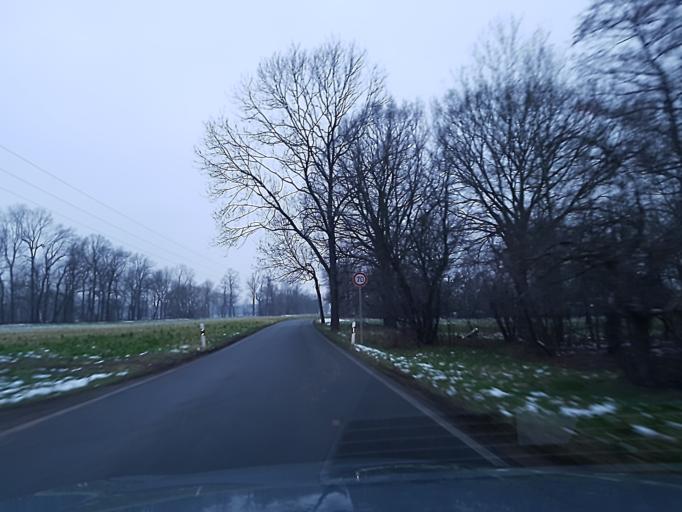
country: DE
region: Saxony
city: Stauchitz
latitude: 51.2587
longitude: 13.2212
